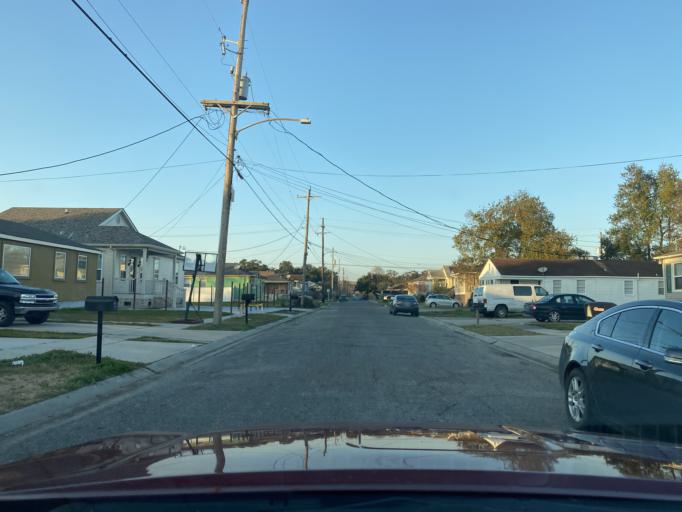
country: US
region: Louisiana
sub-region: Orleans Parish
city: New Orleans
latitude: 30.0208
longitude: -90.0494
